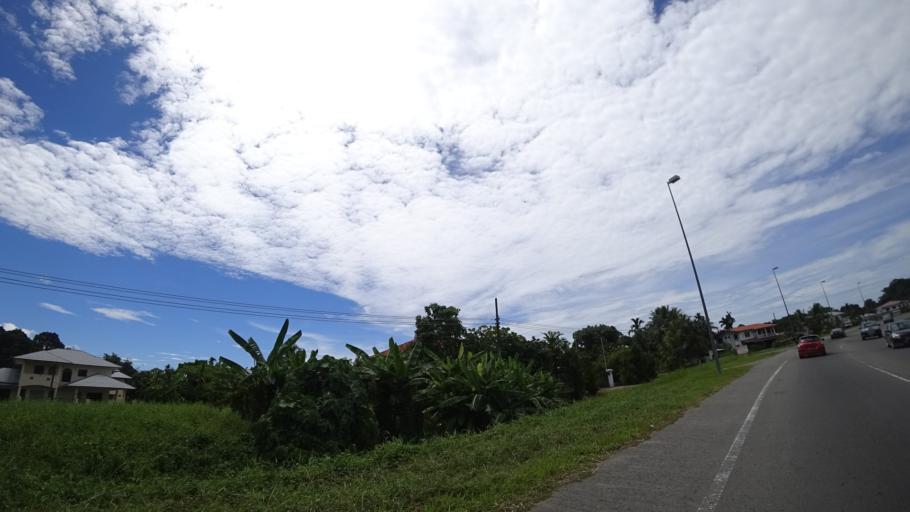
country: MY
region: Sarawak
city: Limbang
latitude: 4.8038
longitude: 114.8325
